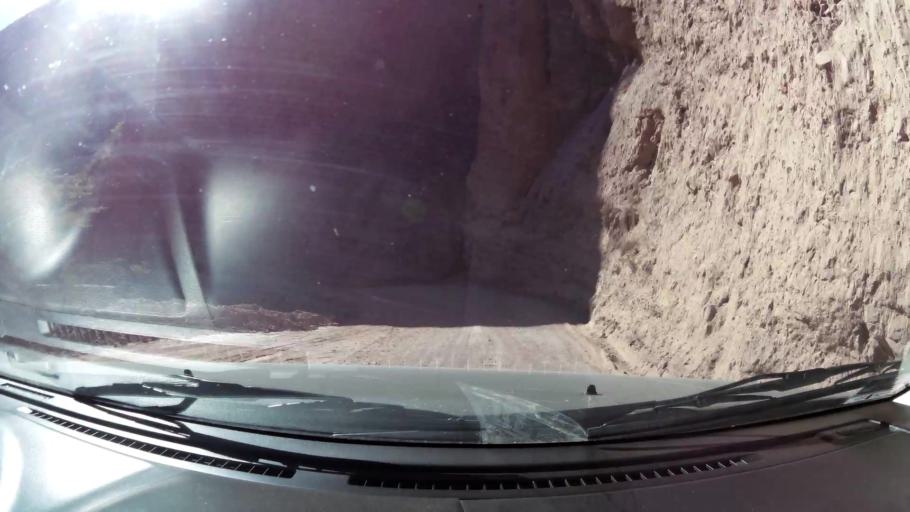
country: PE
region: Huancavelica
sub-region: Provincia de Acobamba
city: Pomacocha
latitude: -12.7852
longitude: -74.4896
